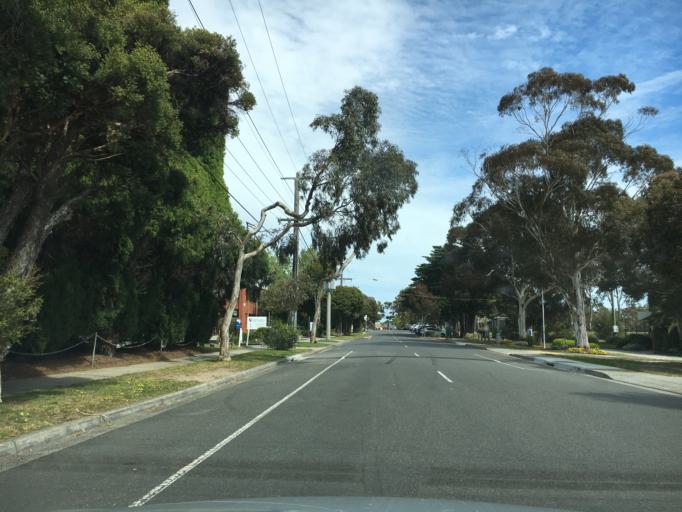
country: AU
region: Victoria
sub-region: Monash
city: Chadstone
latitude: -37.8936
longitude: 145.1007
